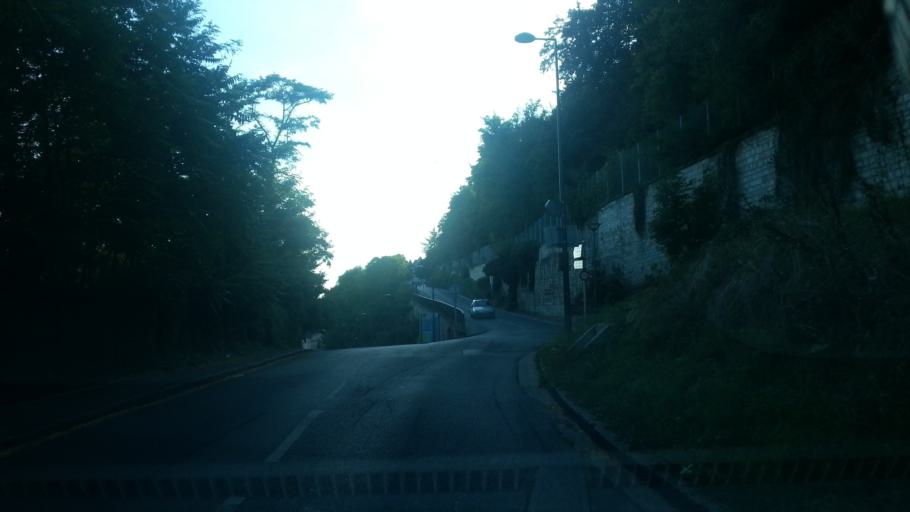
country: FR
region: Picardie
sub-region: Departement de l'Oise
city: Montataire
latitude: 49.2593
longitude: 2.4465
